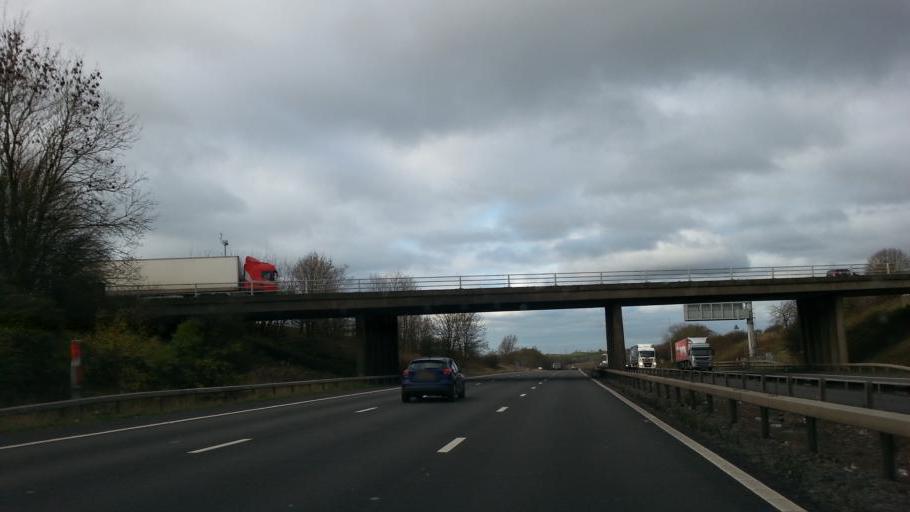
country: GB
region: England
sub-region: Warwickshire
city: Rugby
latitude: 52.4080
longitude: -1.2454
